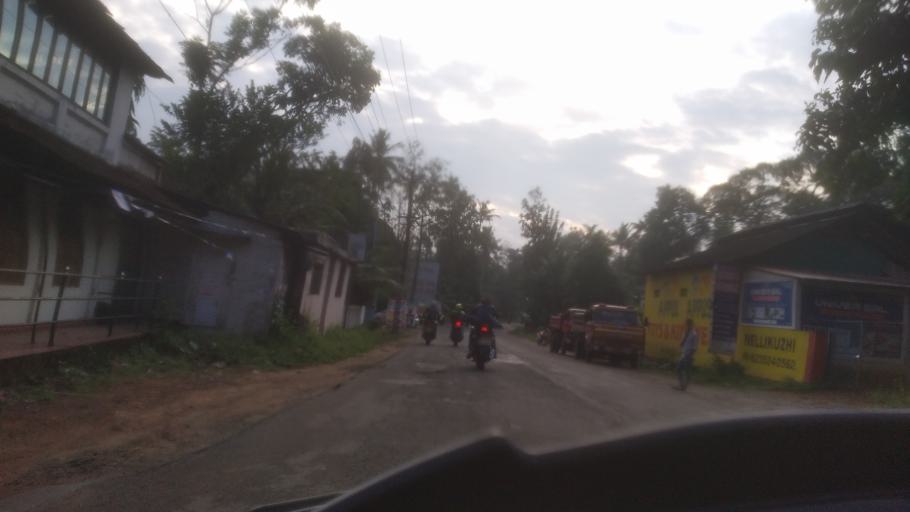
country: IN
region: Kerala
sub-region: Ernakulam
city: Perumpavur
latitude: 10.1046
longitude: 76.5382
